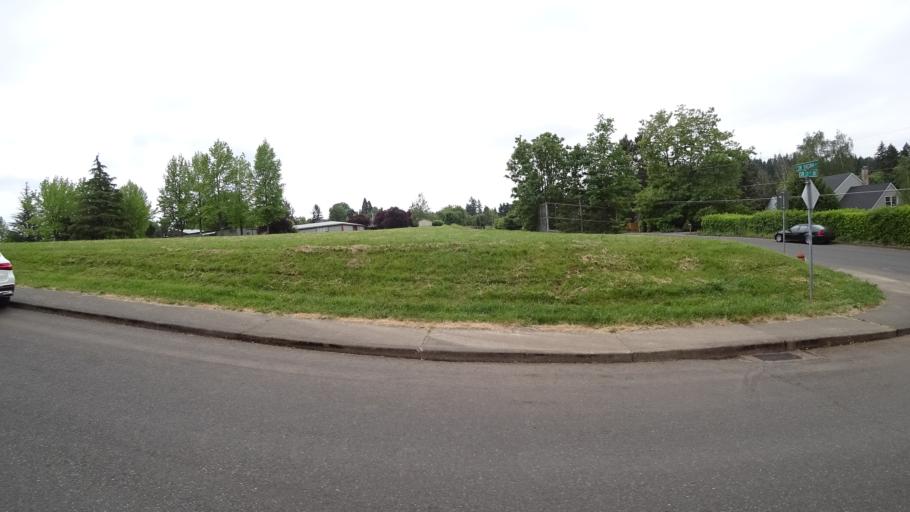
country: US
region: Oregon
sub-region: Clackamas County
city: Lake Oswego
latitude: 45.4420
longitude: -122.7049
